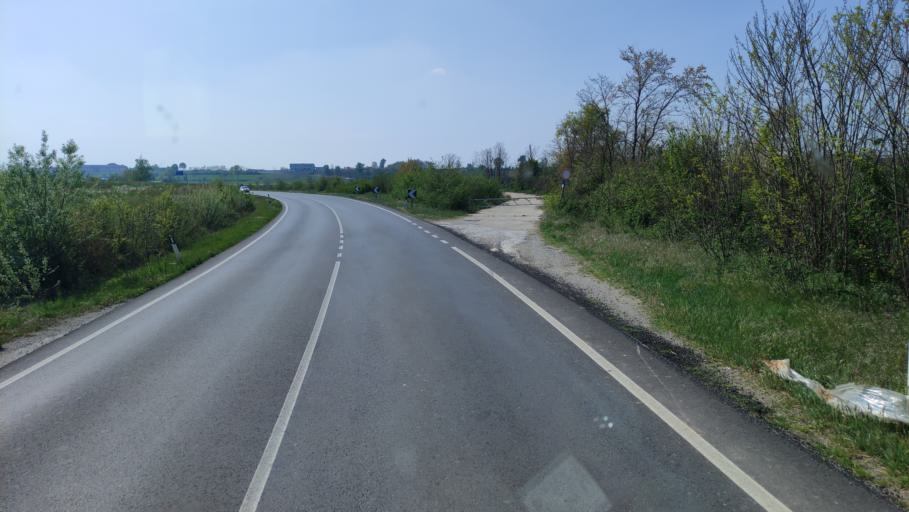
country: IT
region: Piedmont
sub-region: Provincia di Cuneo
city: Marene
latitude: 44.6672
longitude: 7.7631
